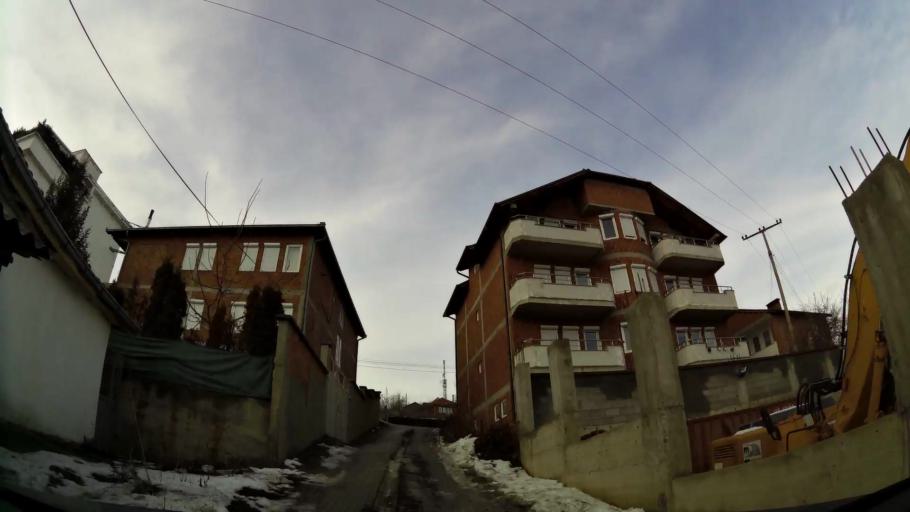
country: XK
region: Pristina
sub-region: Komuna e Prishtines
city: Pristina
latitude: 42.6720
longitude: 21.1842
